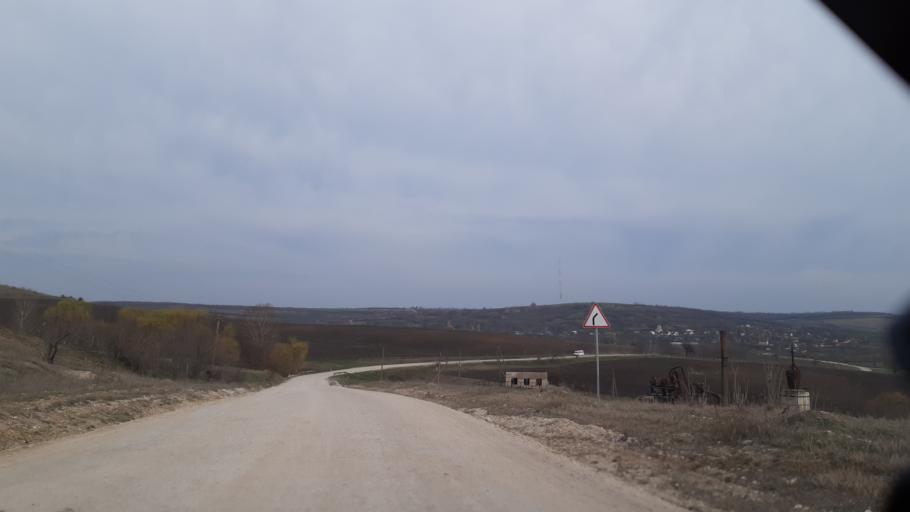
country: MD
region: Soldanesti
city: Soldanesti
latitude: 47.6798
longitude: 28.7852
